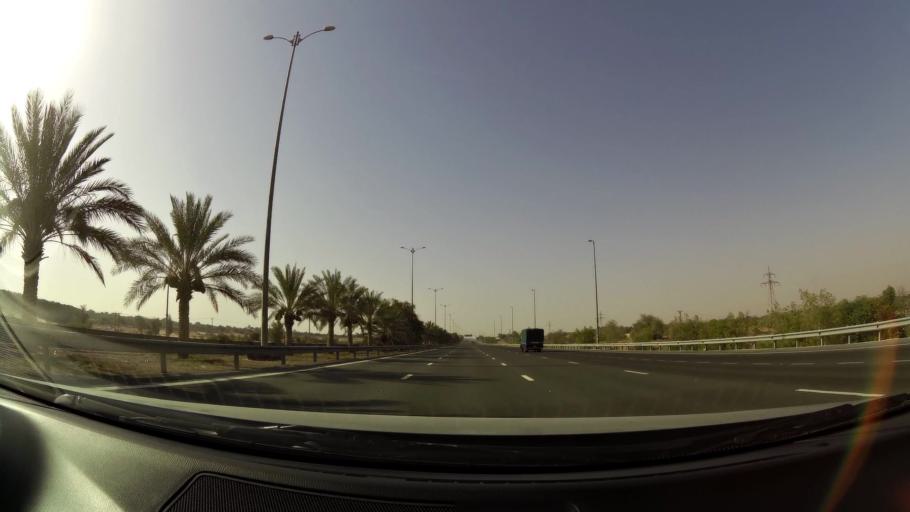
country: OM
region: Al Buraimi
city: Al Buraymi
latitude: 24.5676
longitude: 55.7490
